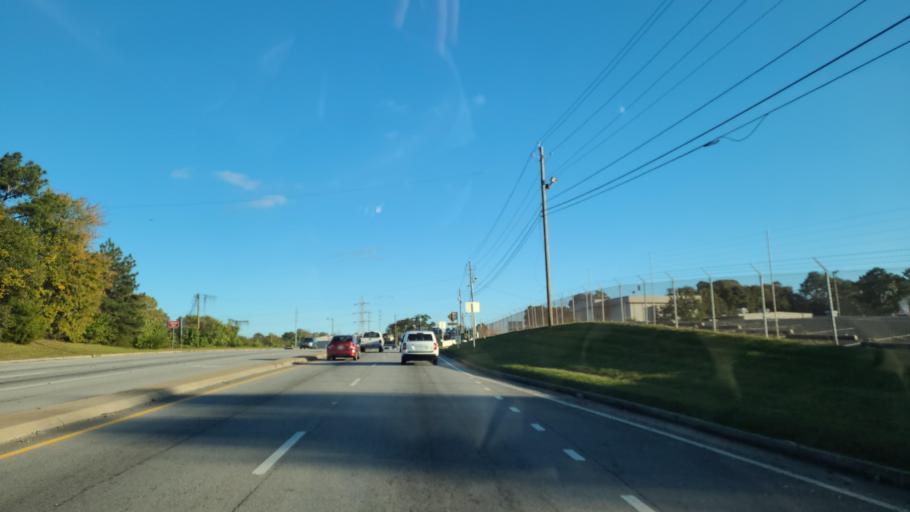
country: US
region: Georgia
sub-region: Clayton County
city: Conley
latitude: 33.6445
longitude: -84.3258
